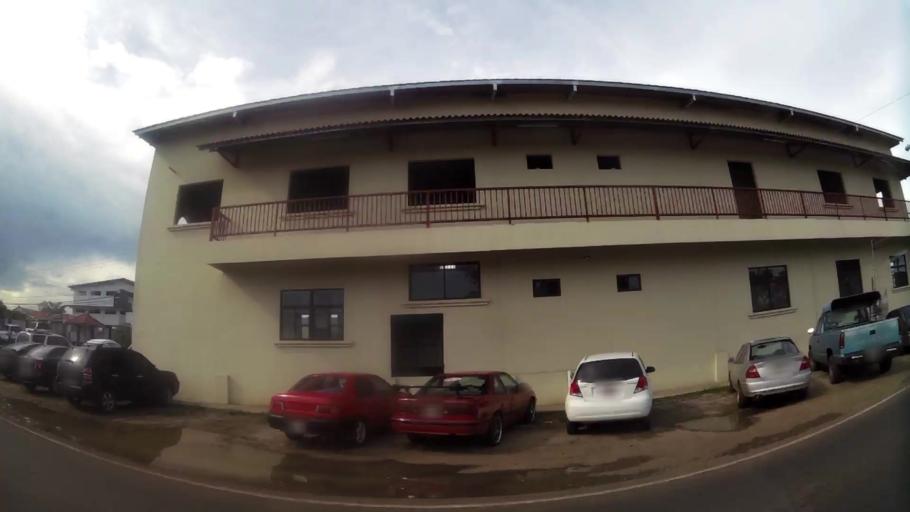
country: PA
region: Panama
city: La Chorrera
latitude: 8.8745
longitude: -79.7901
